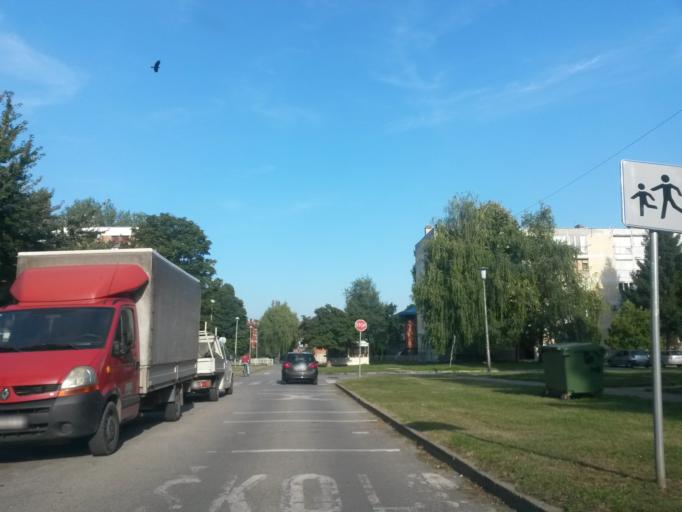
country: HR
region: Osjecko-Baranjska
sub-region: Grad Osijek
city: Osijek
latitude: 45.5448
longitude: 18.7215
